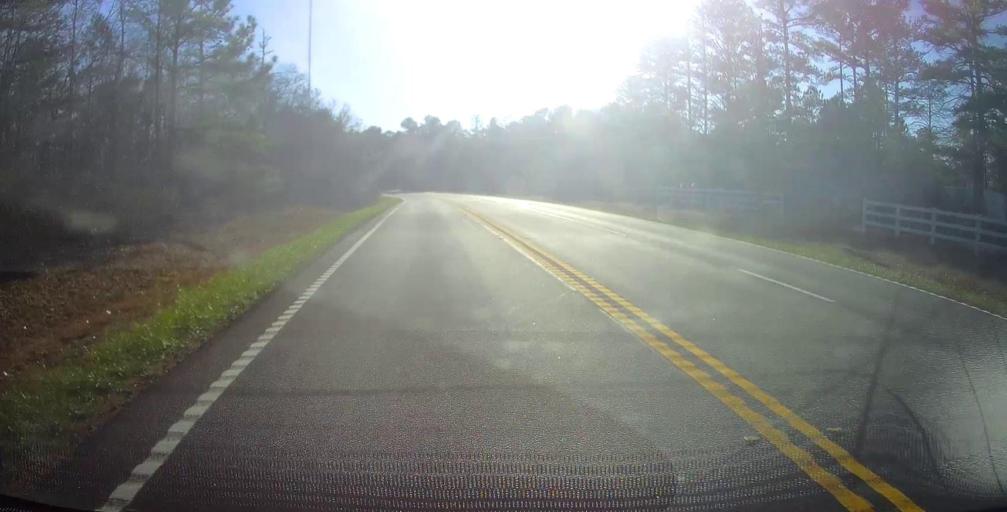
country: US
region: Georgia
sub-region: Meriwether County
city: Manchester
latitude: 32.8558
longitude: -84.6979
